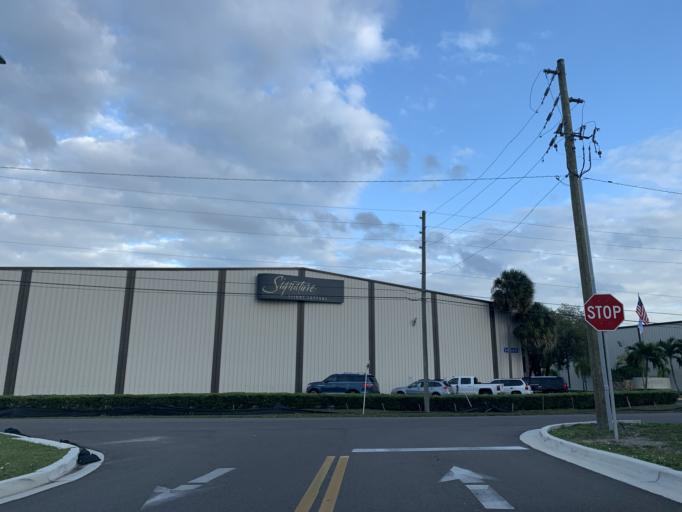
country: US
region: Florida
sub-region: Pinellas County
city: South Highpoint
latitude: 27.9045
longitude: -82.6913
